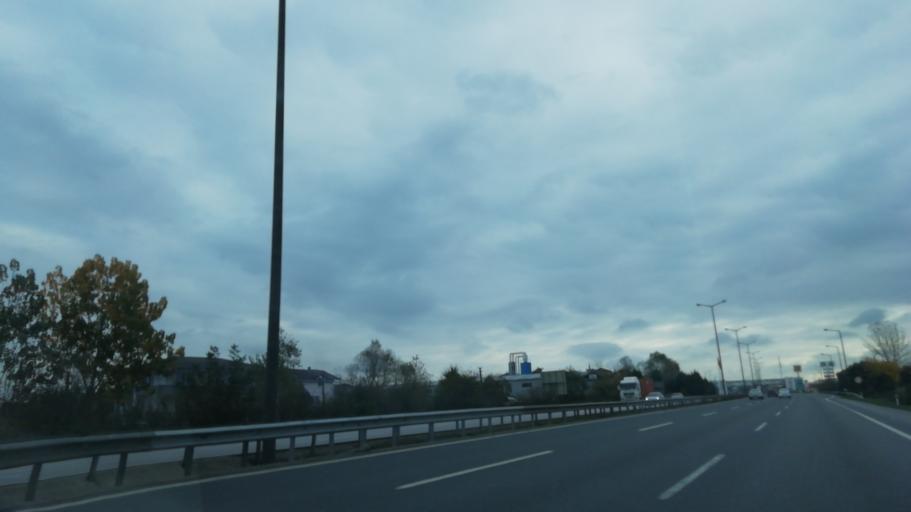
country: TR
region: Kocaeli
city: Derbent
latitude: 40.7294
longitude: 30.0634
